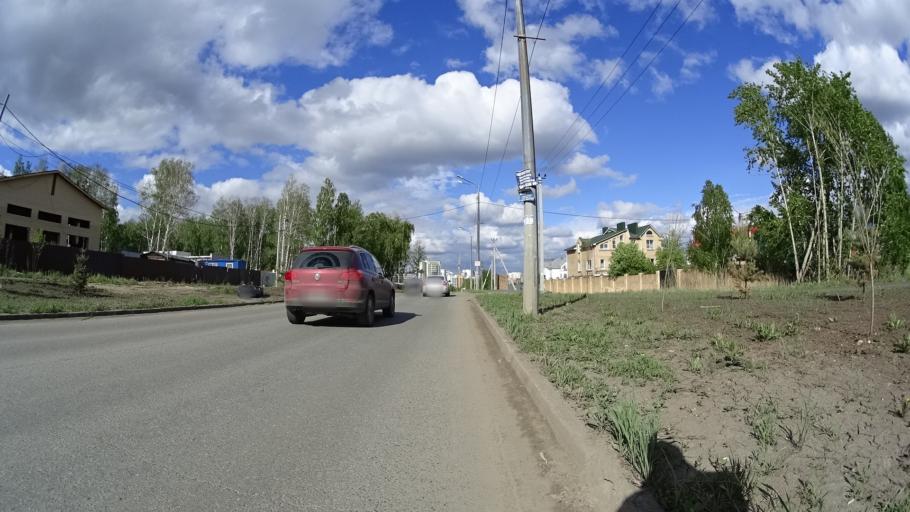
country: RU
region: Chelyabinsk
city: Sargazy
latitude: 55.1556
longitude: 61.2811
